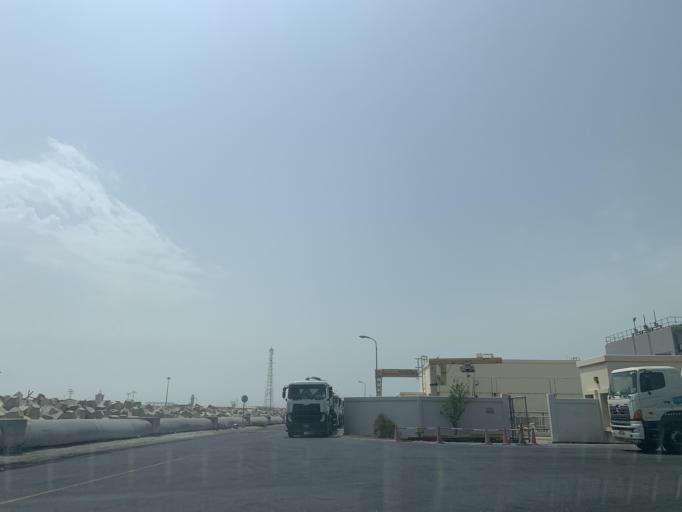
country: BH
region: Muharraq
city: Al Hadd
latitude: 26.2259
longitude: 50.7029
